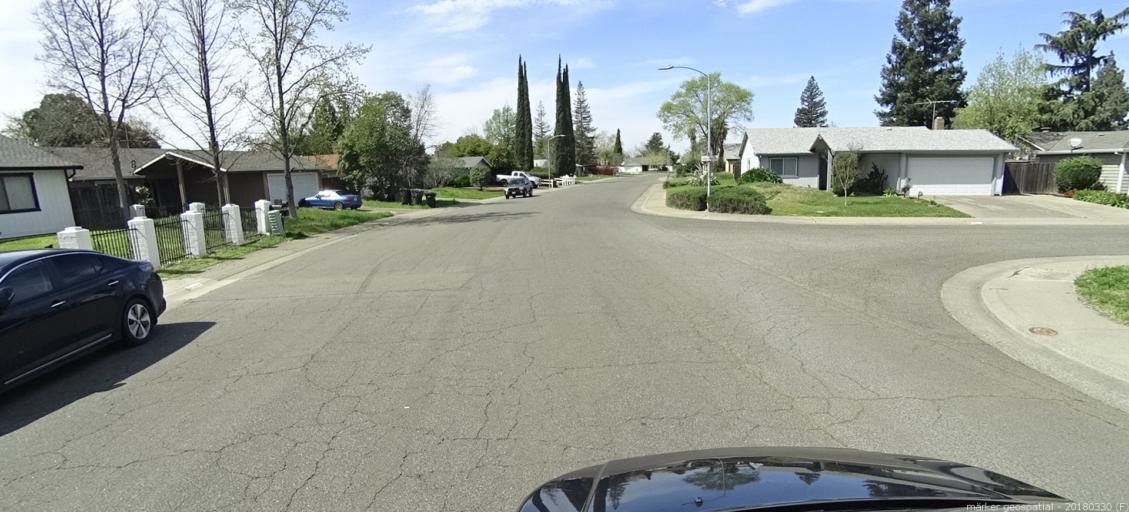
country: US
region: California
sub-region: Sacramento County
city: Rosemont
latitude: 38.5453
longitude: -121.3670
